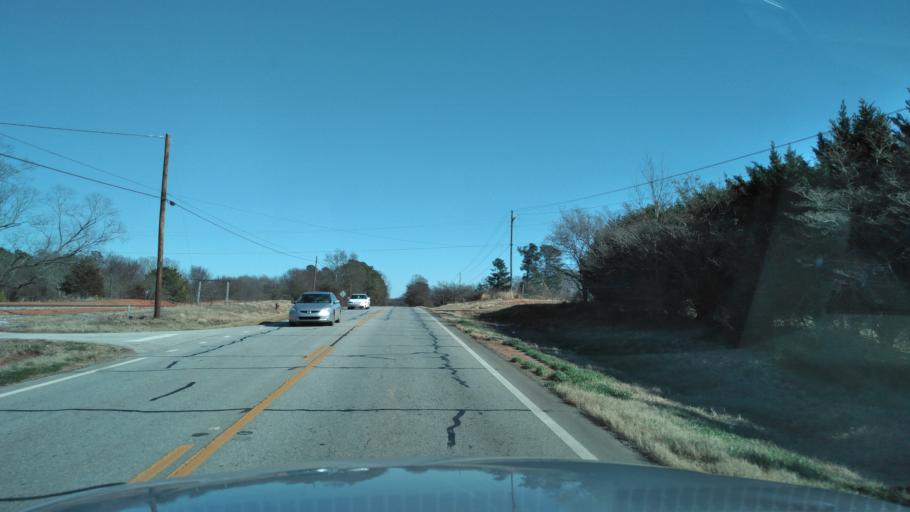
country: US
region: Georgia
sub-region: Banks County
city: Maysville
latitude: 34.2415
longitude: -83.5286
